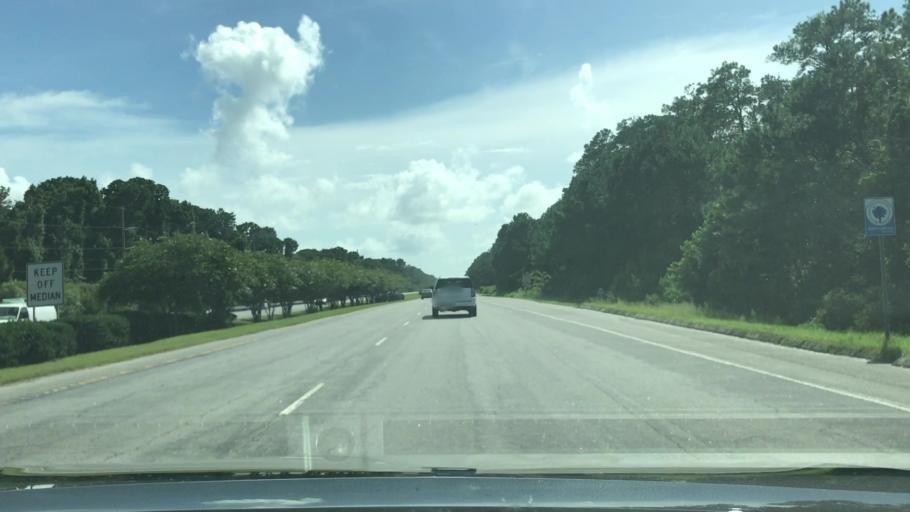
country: US
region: South Carolina
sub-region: Beaufort County
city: Hilton Head Island
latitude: 32.2088
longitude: -80.7408
